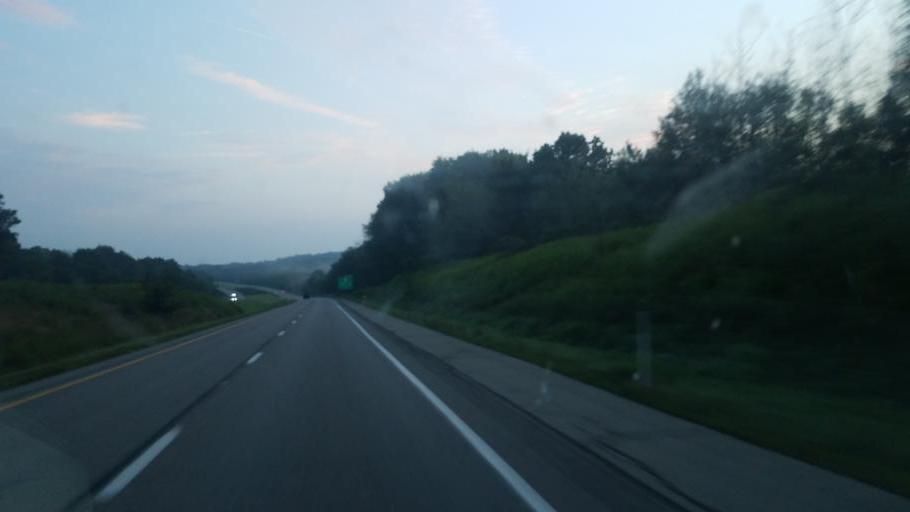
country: US
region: Pennsylvania
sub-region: Mercer County
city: Stoneboro
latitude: 41.3626
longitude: -80.1580
